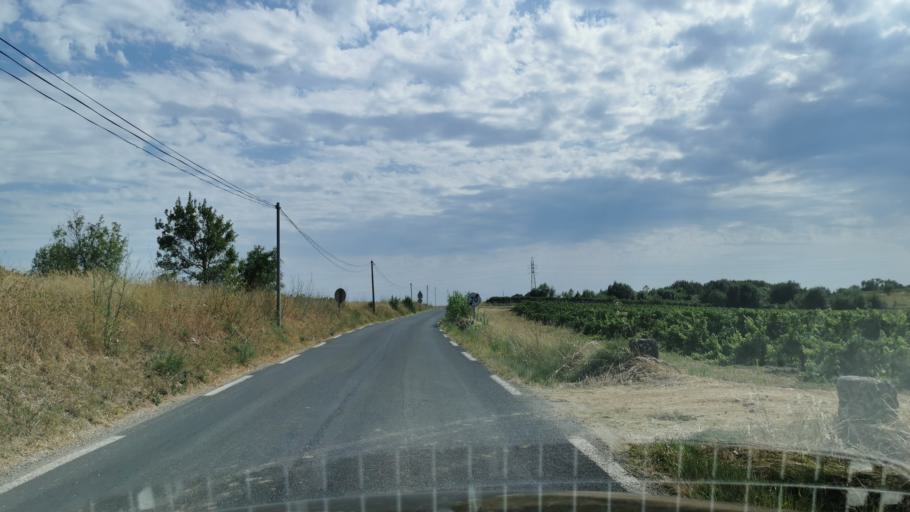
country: FR
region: Languedoc-Roussillon
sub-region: Departement de l'Herault
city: Cazouls-les-Beziers
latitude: 43.3805
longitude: 3.1003
